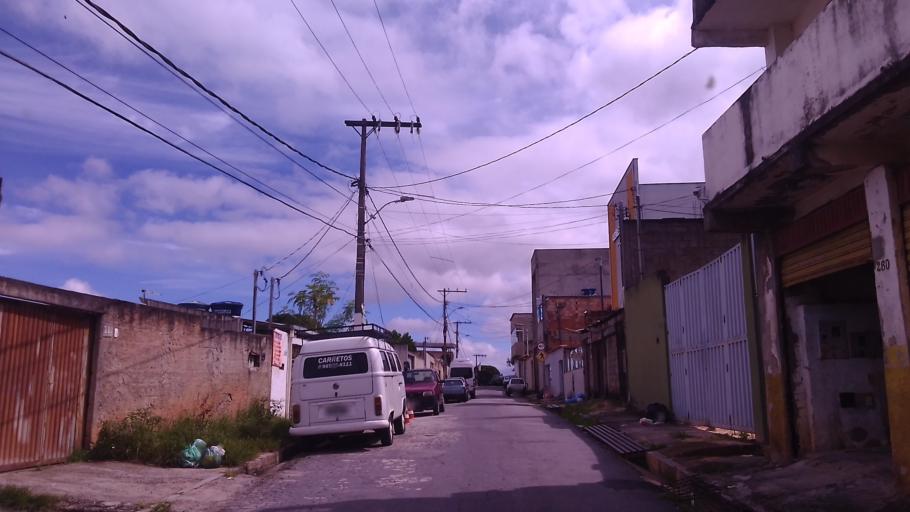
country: BR
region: Minas Gerais
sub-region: Santa Luzia
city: Santa Luzia
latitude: -19.8359
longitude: -43.8929
